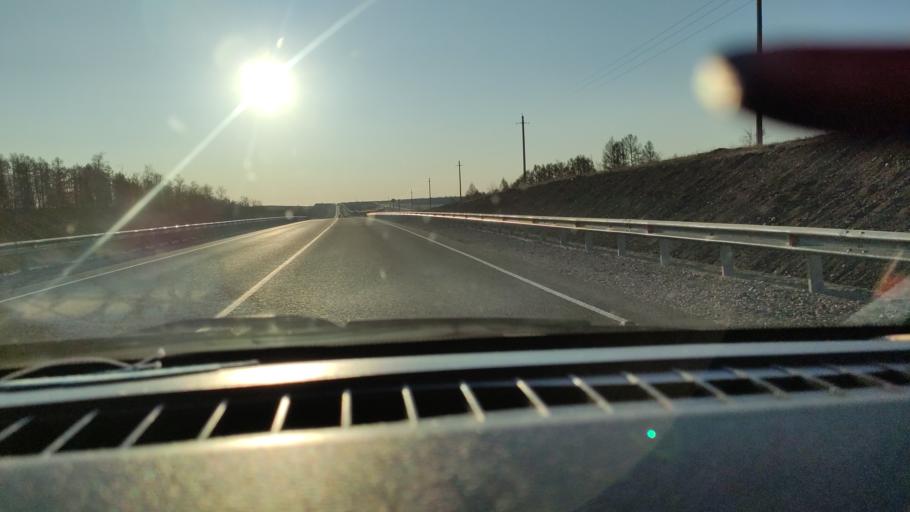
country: RU
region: Saratov
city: Shikhany
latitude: 52.1611
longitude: 47.1162
